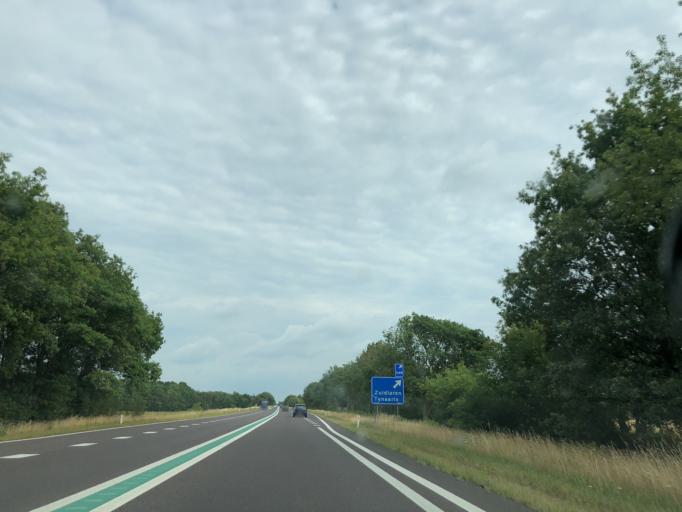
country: NL
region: Drenthe
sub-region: Gemeente Tynaarlo
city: Tynaarlo
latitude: 53.0893
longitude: 6.6464
